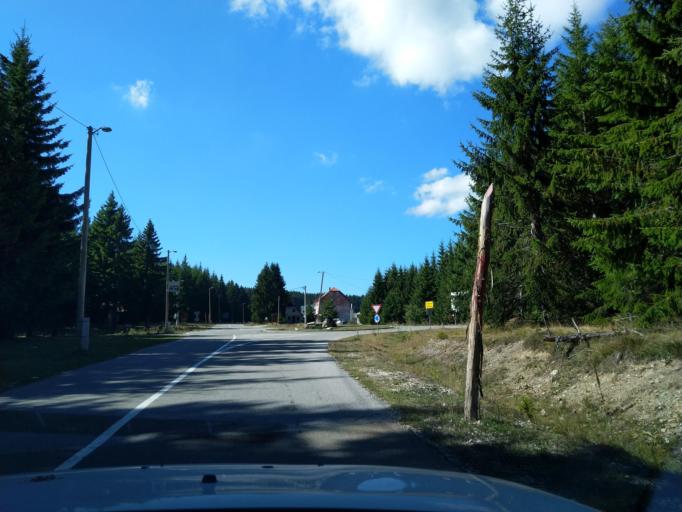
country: RS
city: Sokolovica
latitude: 43.2762
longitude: 20.3451
